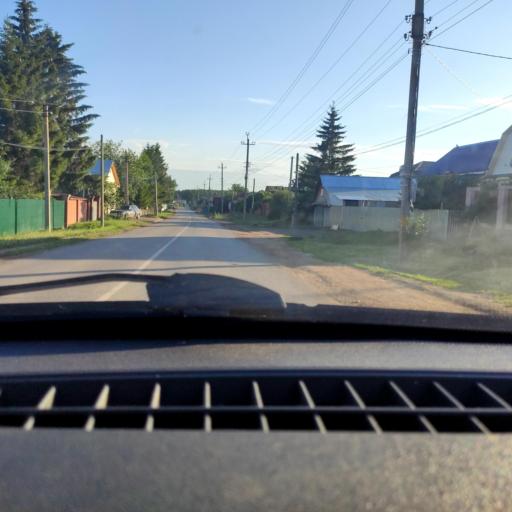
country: RU
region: Bashkortostan
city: Avdon
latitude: 54.6208
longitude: 55.6548
